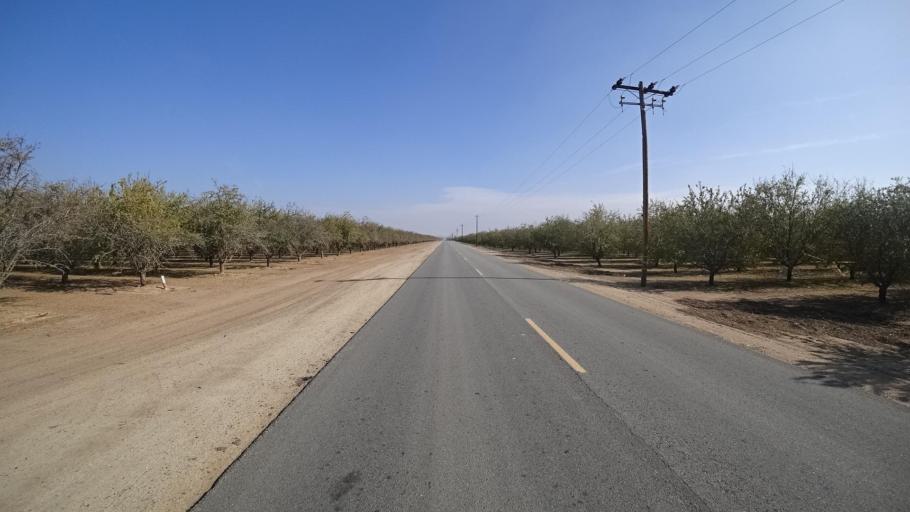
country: US
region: California
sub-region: Kern County
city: Shafter
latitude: 35.5297
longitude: -119.1673
